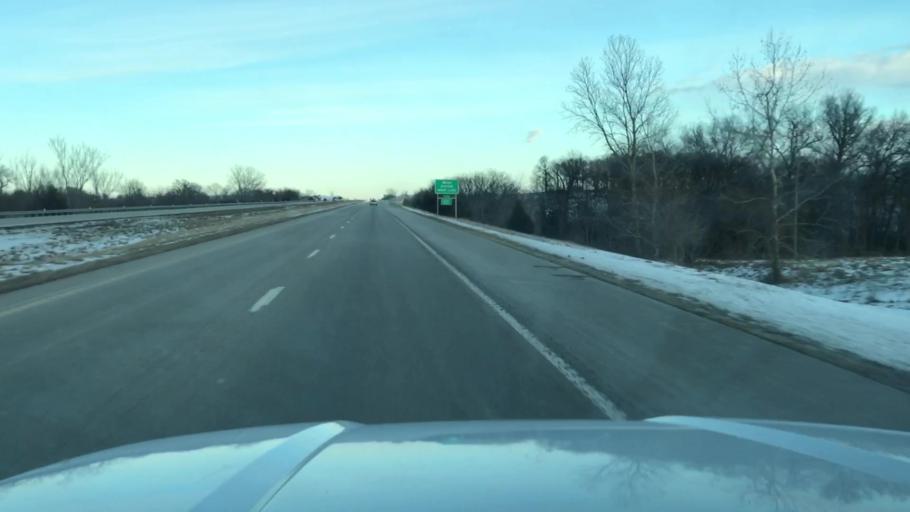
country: US
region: Missouri
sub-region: Buchanan County
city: Saint Joseph
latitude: 39.7476
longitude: -94.7037
